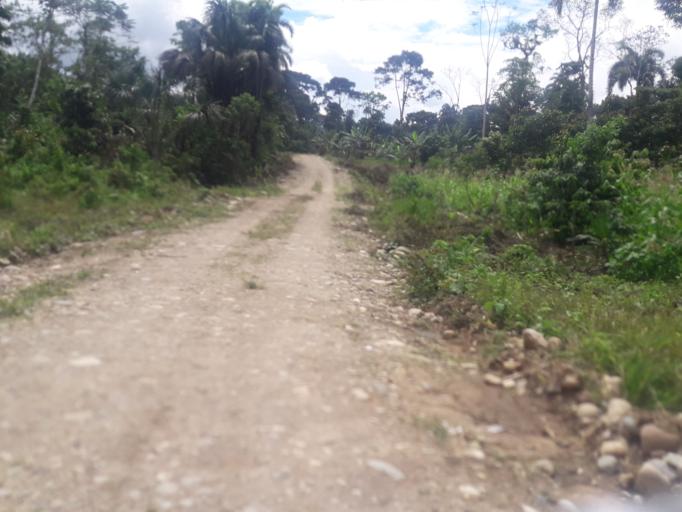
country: EC
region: Napo
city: Tena
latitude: -0.9762
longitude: -77.8515
